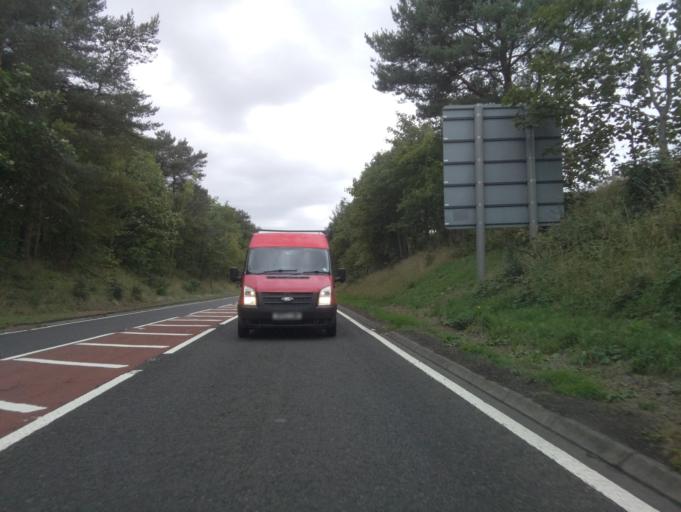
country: GB
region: Scotland
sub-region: Fife
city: High Valleyfield
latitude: 56.0651
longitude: -3.6143
